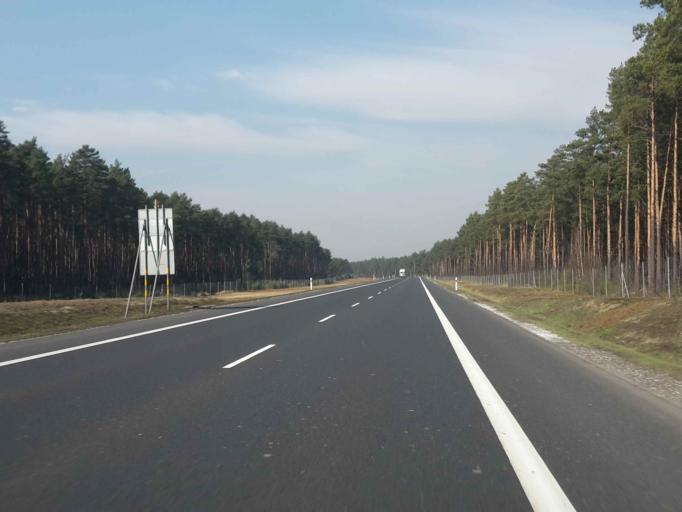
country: PL
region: Kujawsko-Pomorskie
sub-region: Torun
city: Torun
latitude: 52.9710
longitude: 18.6581
